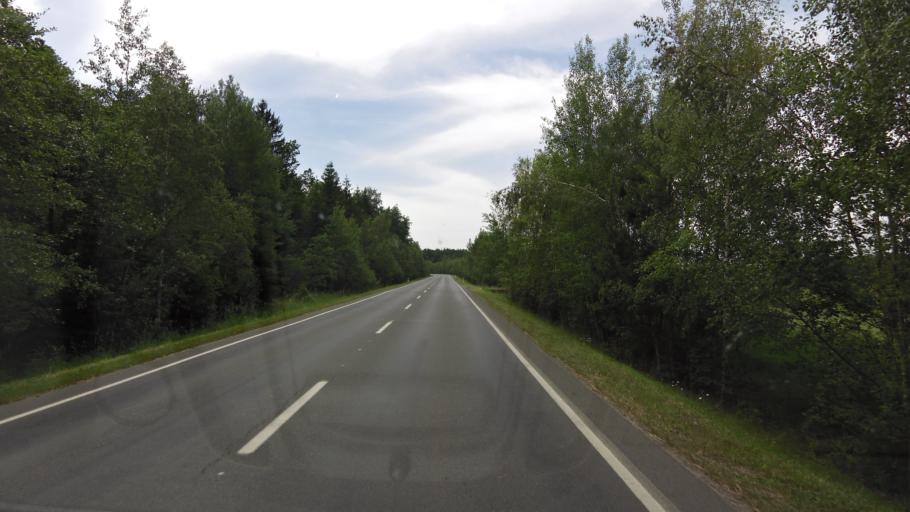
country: CZ
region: Plzensky
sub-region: Okres Rokycany
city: Rokycany
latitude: 49.7145
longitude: 13.5525
